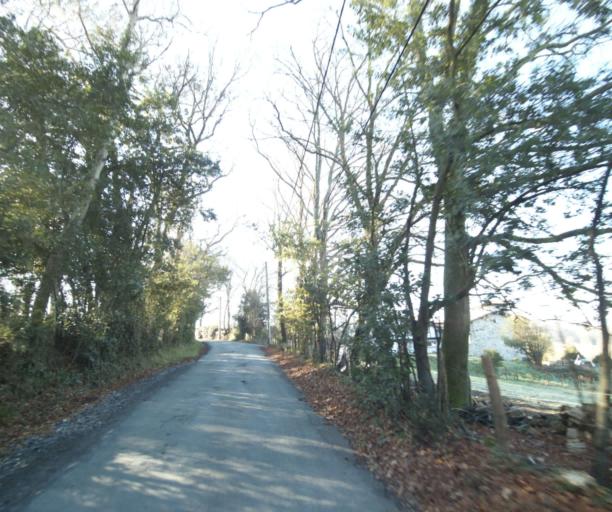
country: FR
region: Aquitaine
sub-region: Departement des Pyrenees-Atlantiques
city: Ciboure
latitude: 43.3701
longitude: -1.6703
